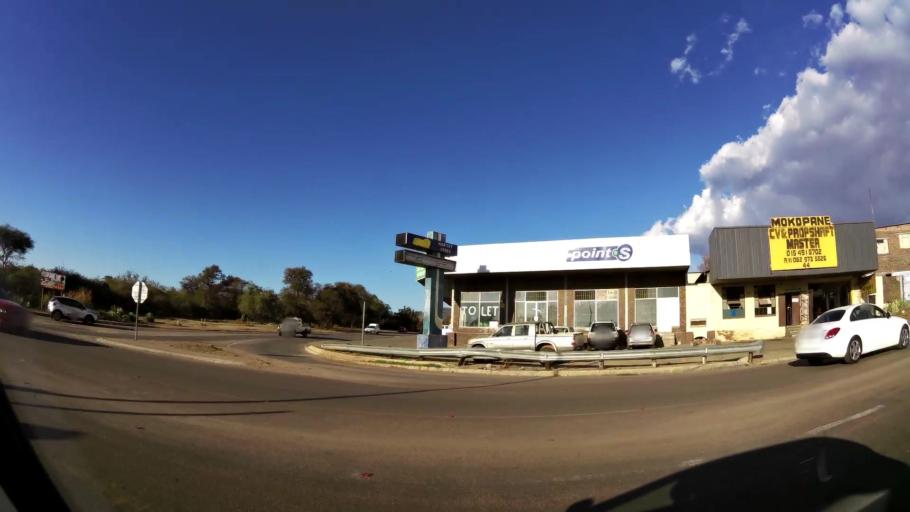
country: ZA
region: Limpopo
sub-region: Waterberg District Municipality
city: Mokopane
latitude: -24.1750
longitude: 29.0019
